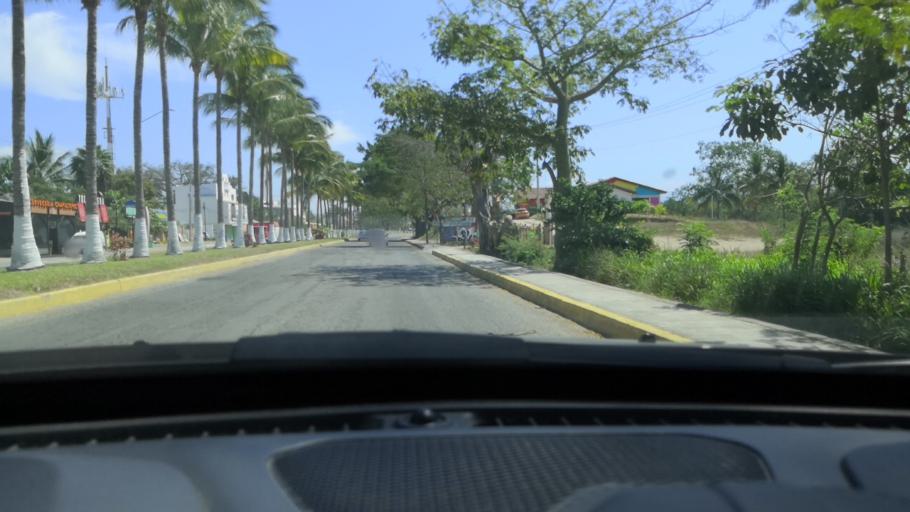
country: MX
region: Nayarit
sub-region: Bahia de Banderas
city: Las Jarretaderas
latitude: 20.7099
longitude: -105.2899
